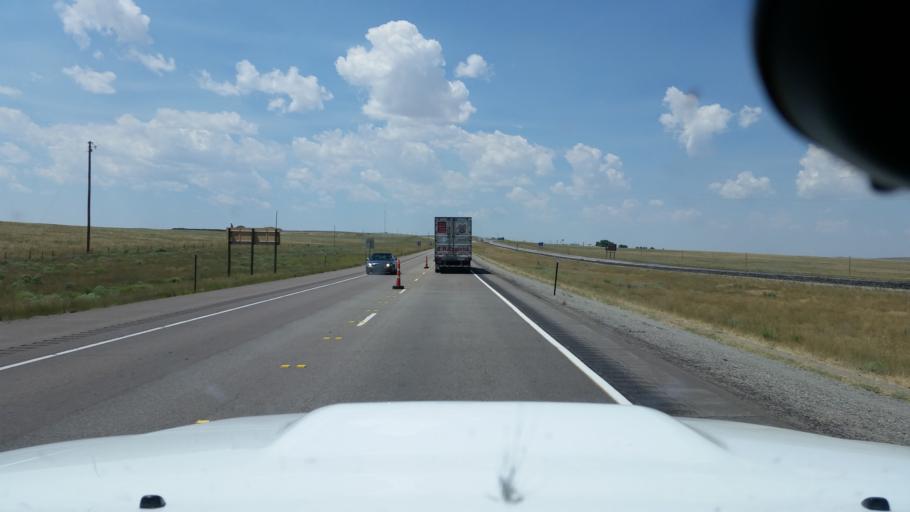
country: US
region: Wyoming
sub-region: Carbon County
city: Saratoga
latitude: 41.7415
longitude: -106.8114
